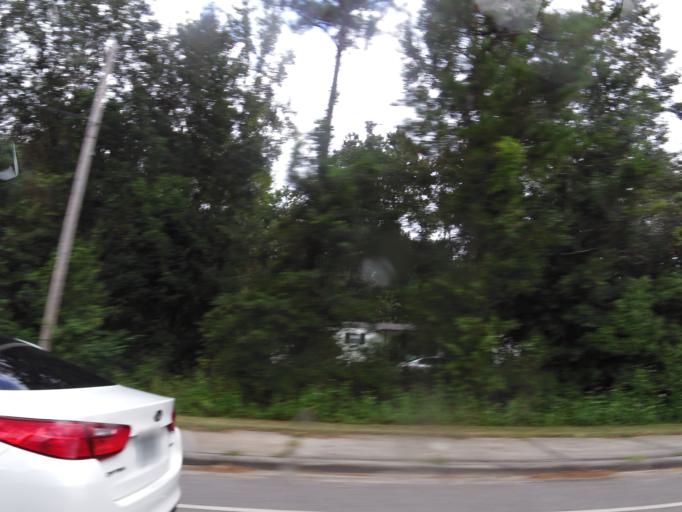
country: US
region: Florida
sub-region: Clay County
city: Lakeside
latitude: 30.1049
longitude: -81.7926
